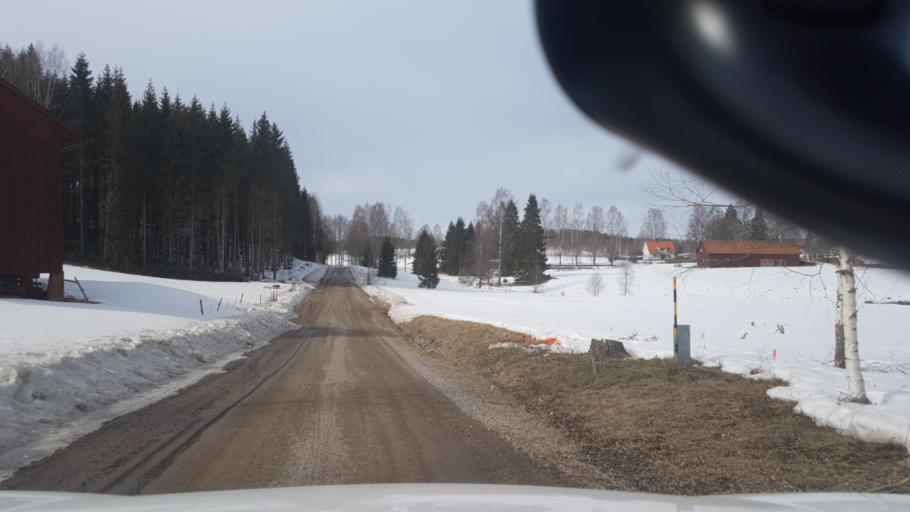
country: SE
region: Vaermland
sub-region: Eda Kommun
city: Charlottenberg
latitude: 59.8429
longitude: 12.3574
